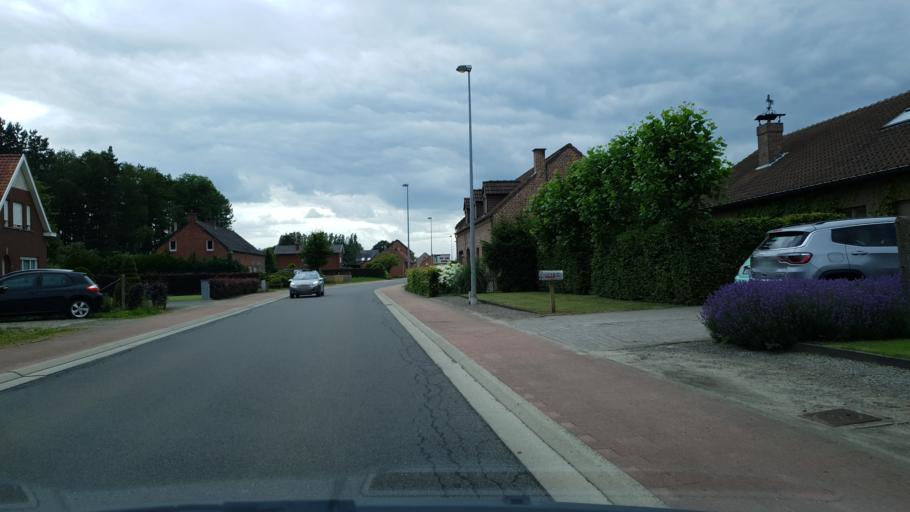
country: BE
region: Flanders
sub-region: Provincie Antwerpen
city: Heist-op-den-Berg
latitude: 51.0508
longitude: 4.7430
